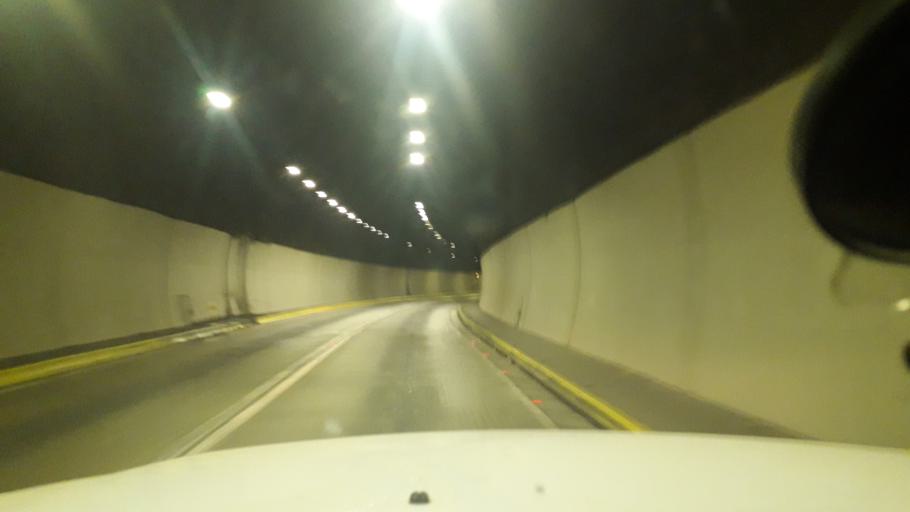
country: CL
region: Valparaiso
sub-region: Provincia de Valparaiso
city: Valparaiso
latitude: -33.0431
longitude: -71.6535
